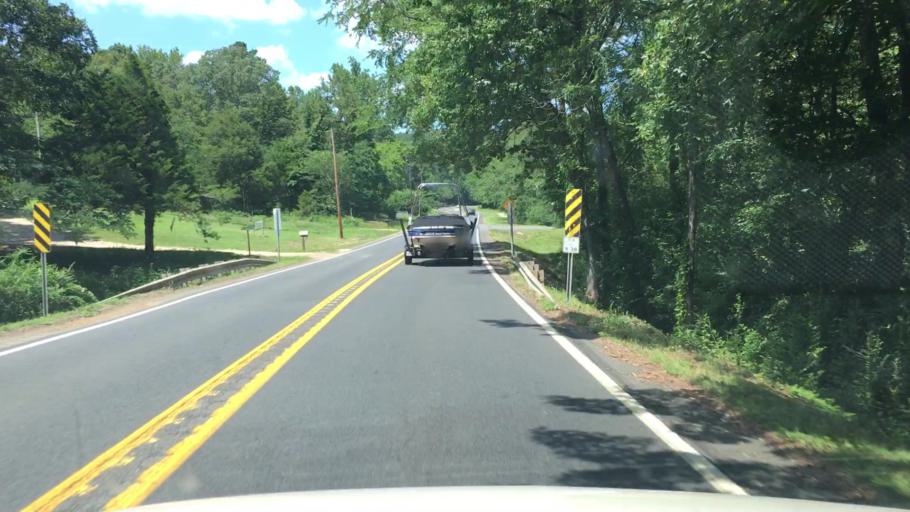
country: US
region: Arkansas
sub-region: Garland County
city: Lake Hamilton
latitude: 34.3478
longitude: -93.1843
